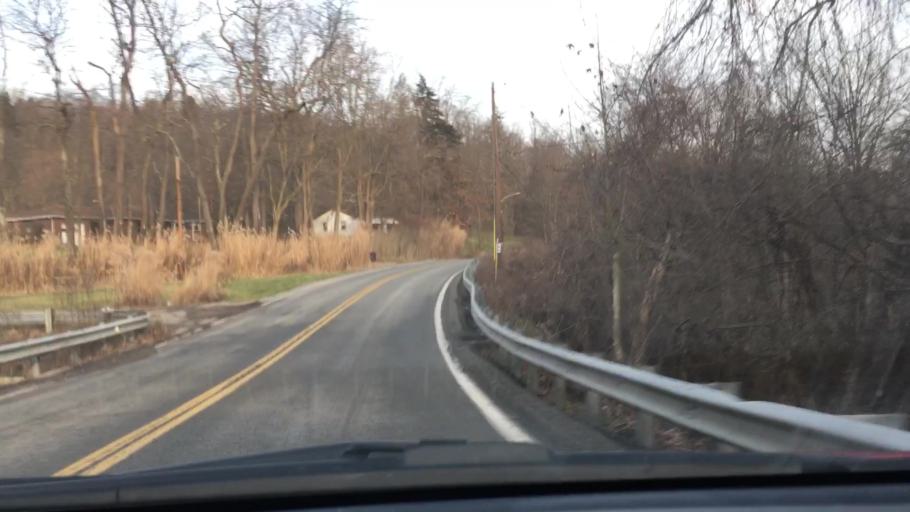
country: US
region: Pennsylvania
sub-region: Allegheny County
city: Elizabeth
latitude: 40.2422
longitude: -79.8445
